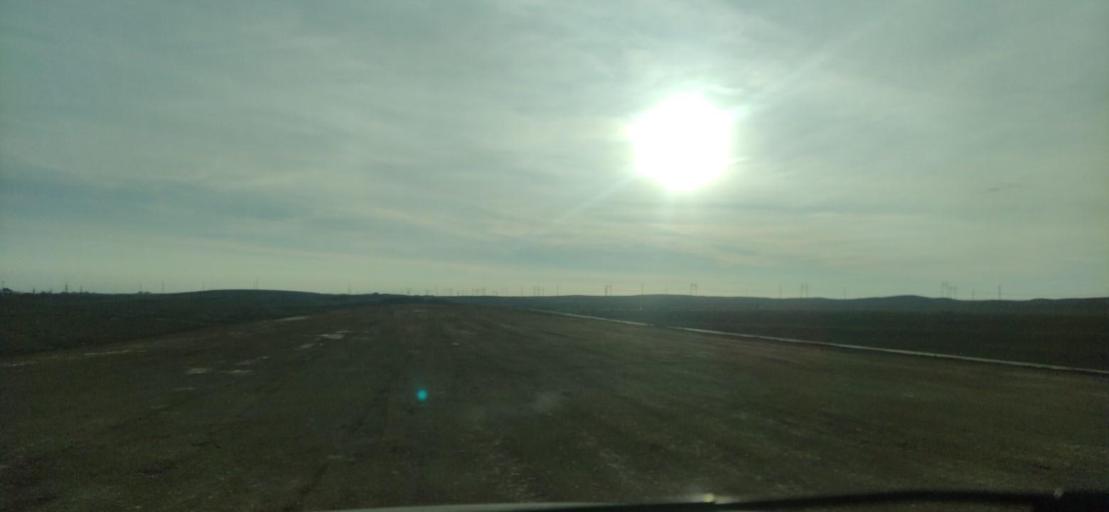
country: KZ
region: Qaraghandy
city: Saryshaghan
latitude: 46.1366
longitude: 73.6037
